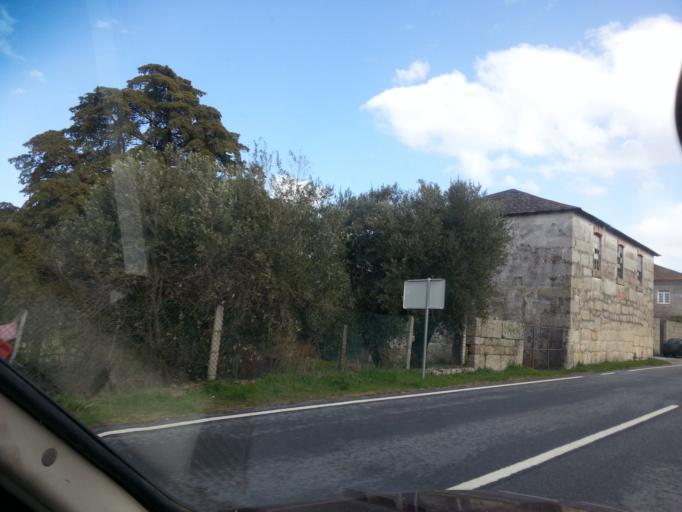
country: PT
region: Guarda
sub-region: Celorico da Beira
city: Celorico da Beira
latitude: 40.6194
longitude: -7.3126
